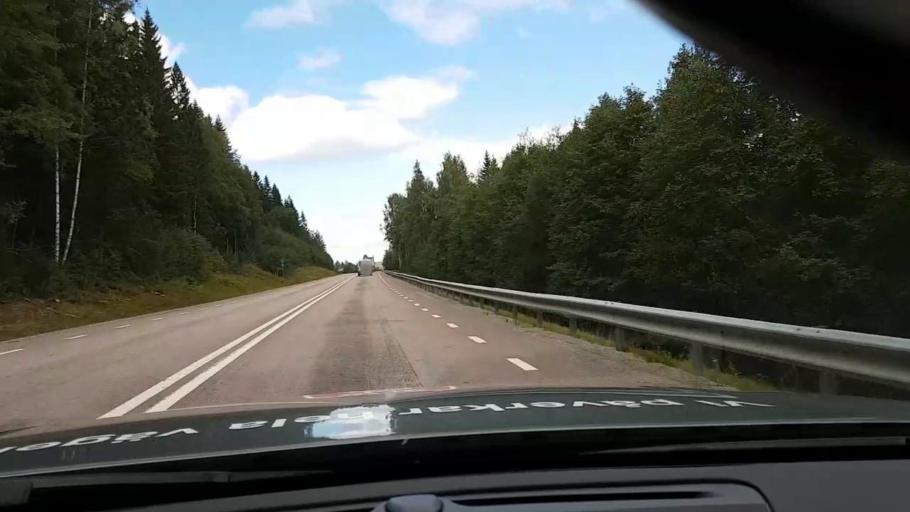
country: SE
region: Vaesternorrland
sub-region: OErnskoeldsviks Kommun
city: Bjasta
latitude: 63.3601
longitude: 18.4662
